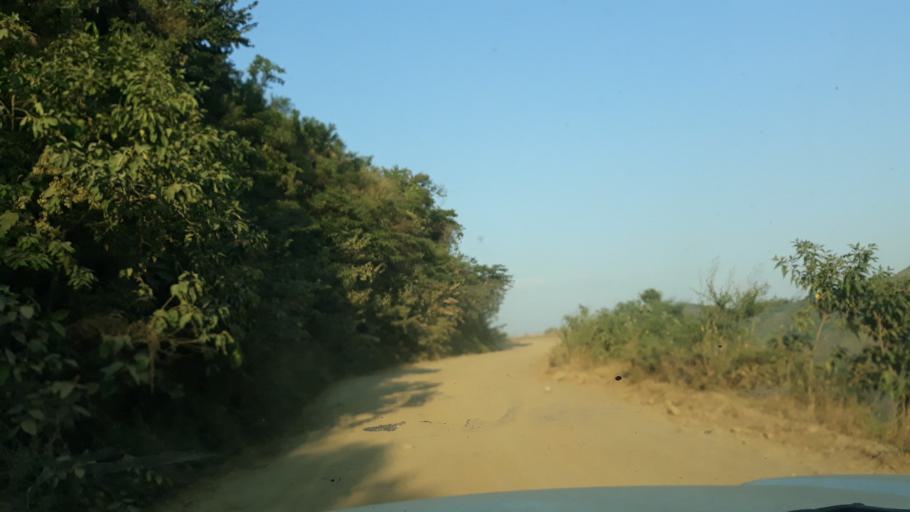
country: RW
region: Western Province
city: Cyangugu
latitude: -2.7048
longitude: 28.9514
